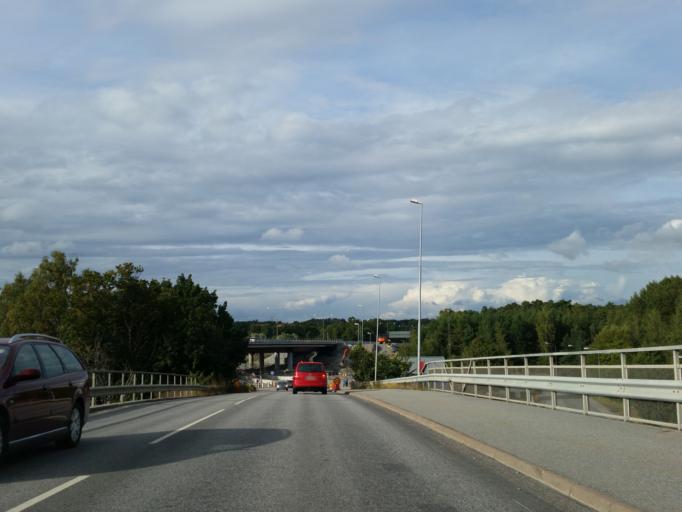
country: SE
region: Stockholm
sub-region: Upplands Vasby Kommun
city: Upplands Vaesby
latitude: 59.4730
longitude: 17.9177
